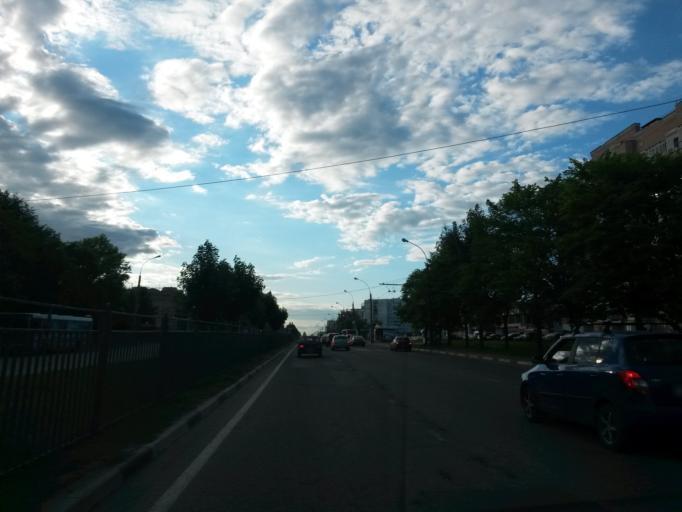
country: RU
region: Jaroslavl
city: Yaroslavl
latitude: 57.6883
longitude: 39.7806
